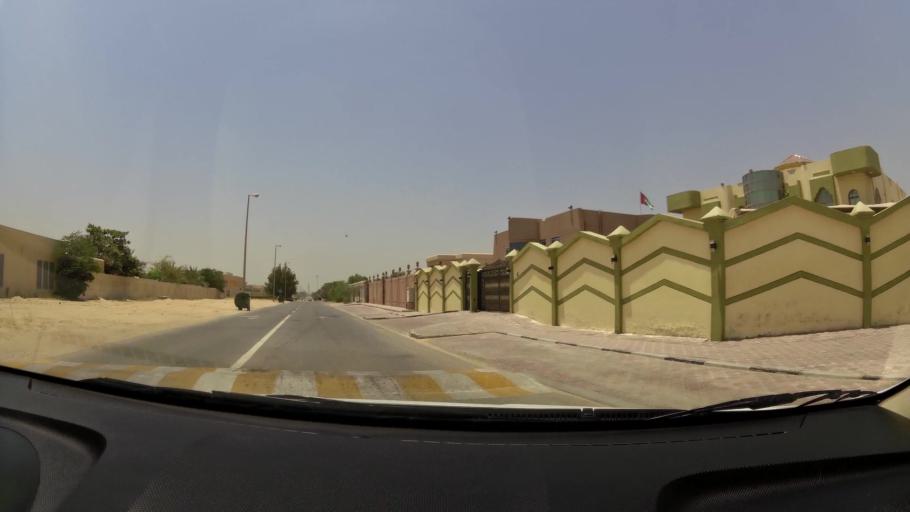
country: AE
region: Ajman
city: Ajman
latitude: 25.4082
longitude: 55.5004
